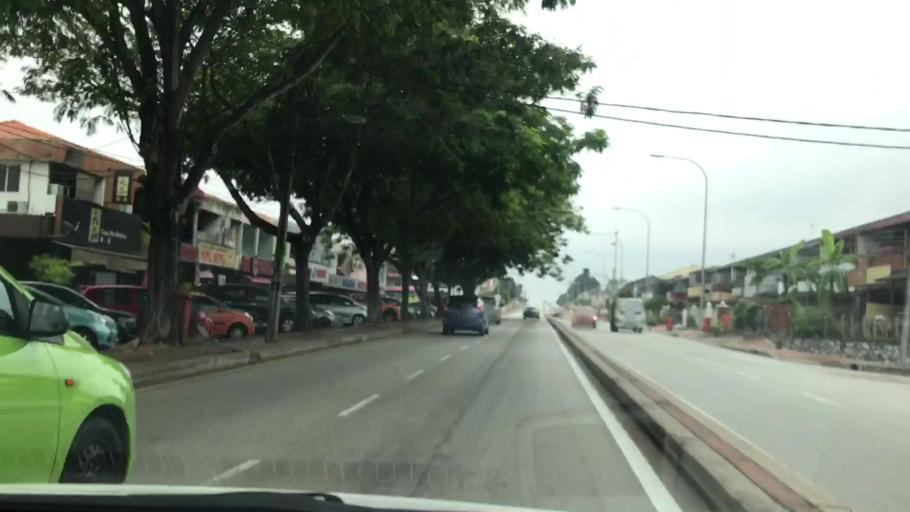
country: MY
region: Selangor
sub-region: Petaling
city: Petaling Jaya
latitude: 3.1141
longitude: 101.6209
